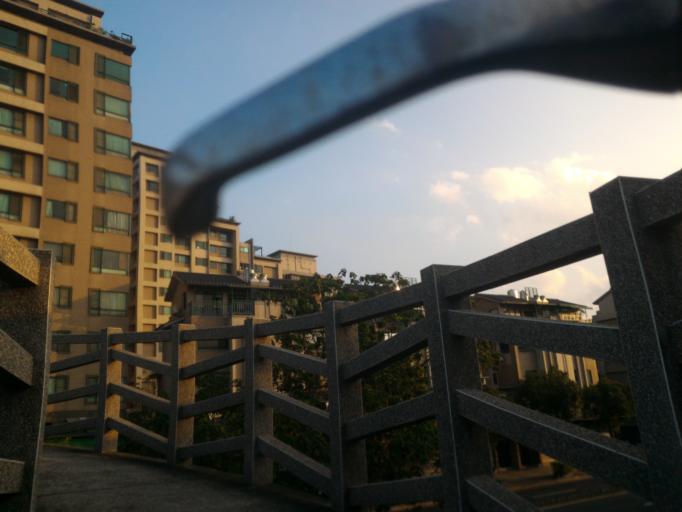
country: TW
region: Taiwan
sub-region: Taoyuan
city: Taoyuan
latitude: 24.9685
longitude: 121.3941
